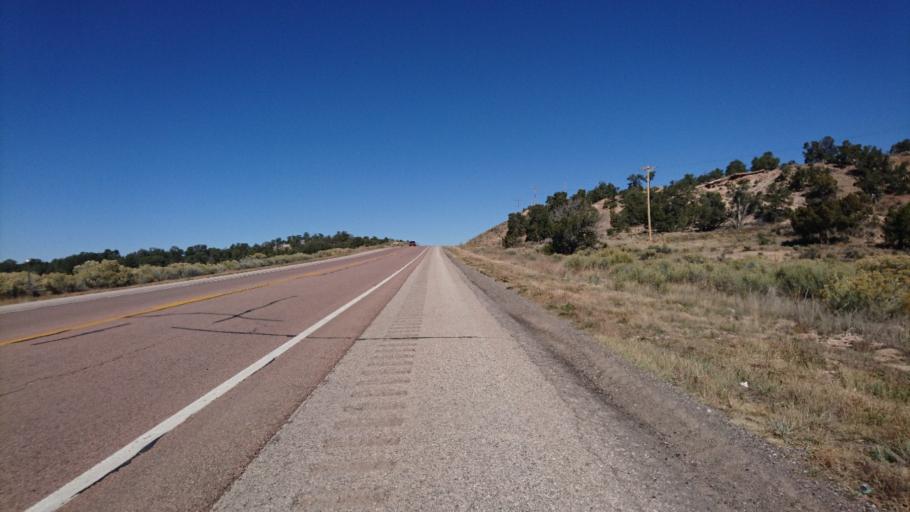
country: US
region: New Mexico
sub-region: McKinley County
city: Gallup
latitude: 35.3417
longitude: -108.7579
